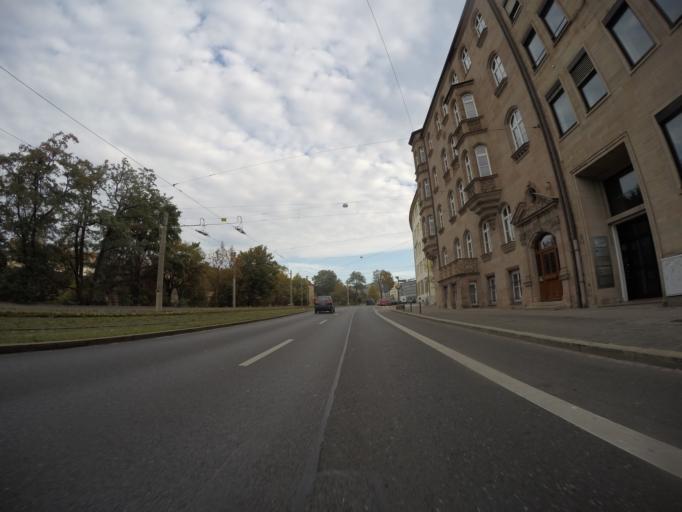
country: DE
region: Bavaria
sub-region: Regierungsbezirk Mittelfranken
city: Nuernberg
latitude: 49.4541
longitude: 11.0874
